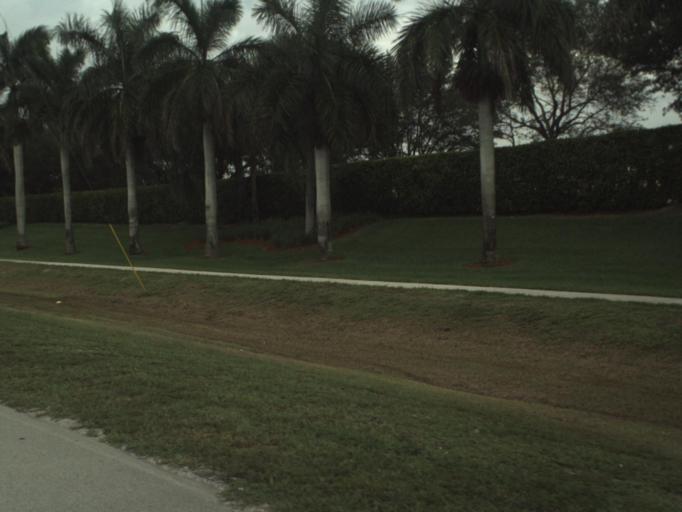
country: US
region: Florida
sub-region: Palm Beach County
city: Royal Palm Beach
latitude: 26.7091
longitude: -80.1864
